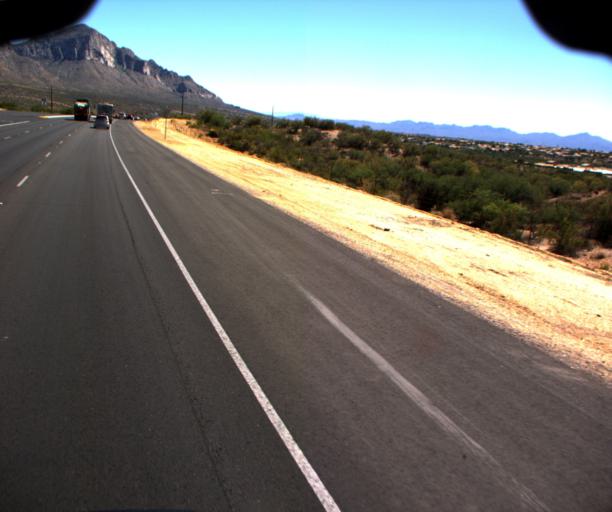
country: US
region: Arizona
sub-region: Pima County
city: Oro Valley
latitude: 32.4307
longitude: -110.9343
